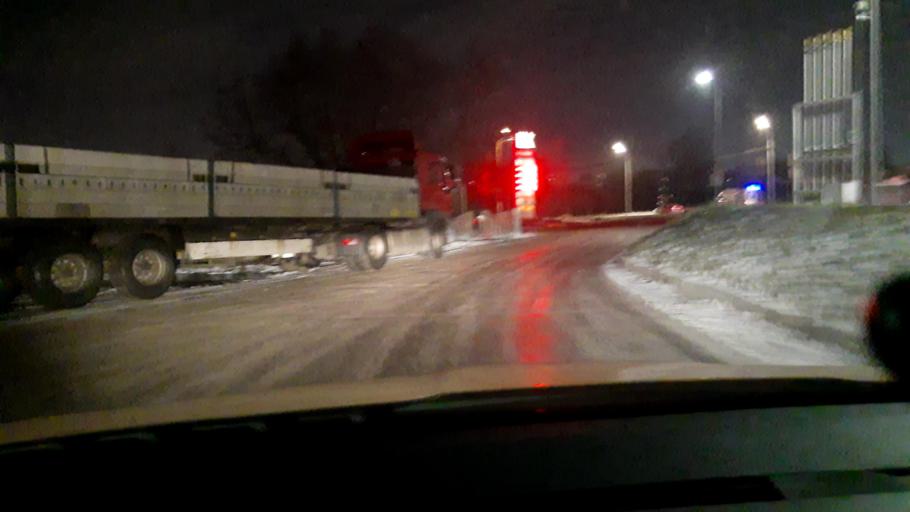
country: RU
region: Moscow
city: Kapotnya
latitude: 55.6577
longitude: 37.7887
